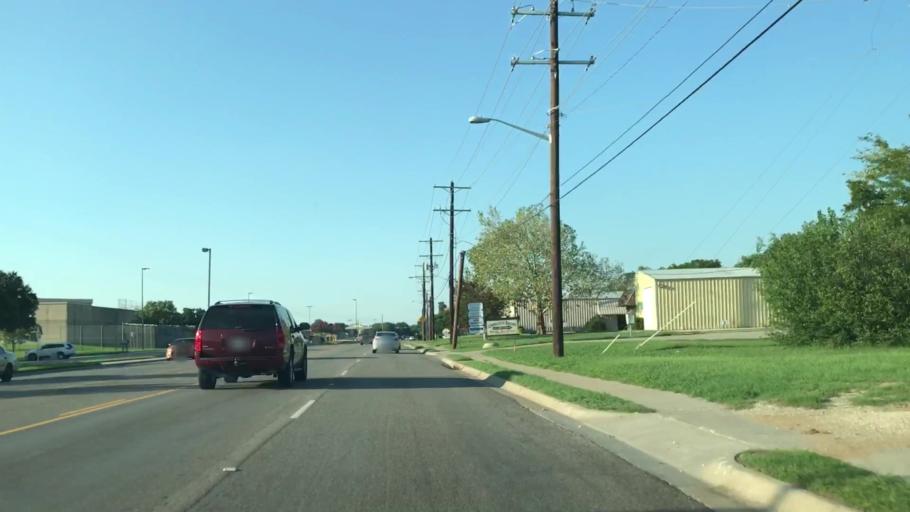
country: US
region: Texas
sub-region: Denton County
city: Denton
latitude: 33.2117
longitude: -97.1119
